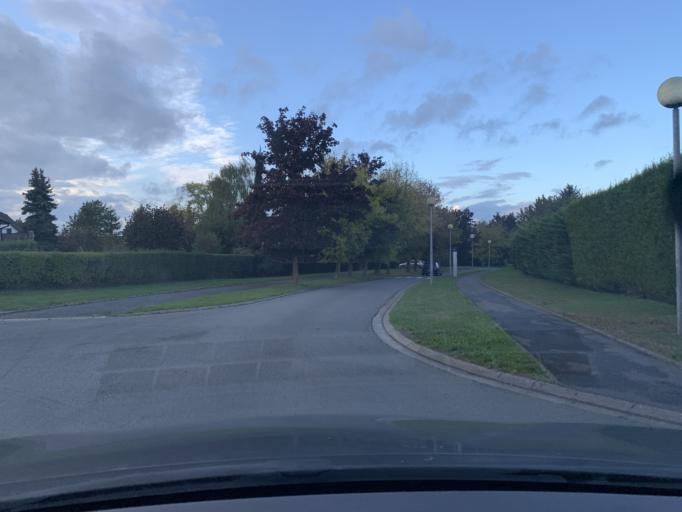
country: FR
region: Nord-Pas-de-Calais
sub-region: Departement du Nord
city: Proville
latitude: 50.1570
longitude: 3.2107
